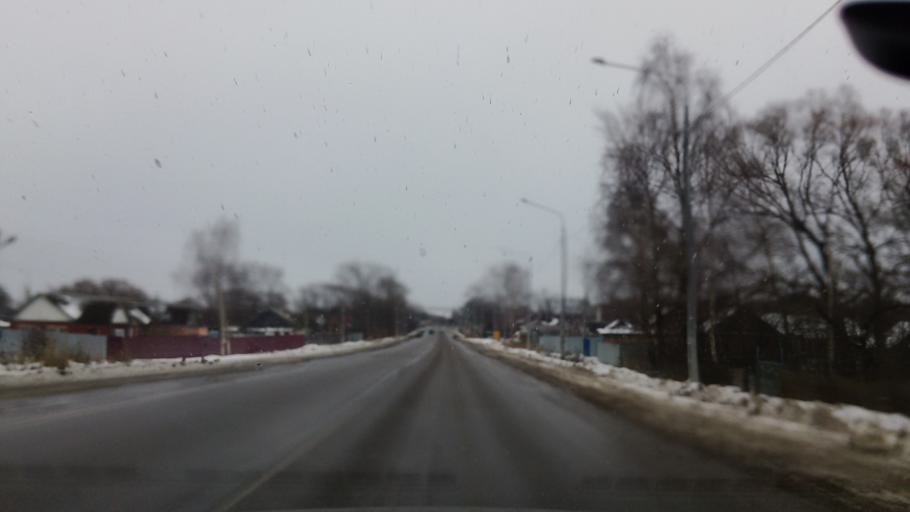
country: RU
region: Tula
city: Bolokhovo
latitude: 54.0524
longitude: 37.8151
